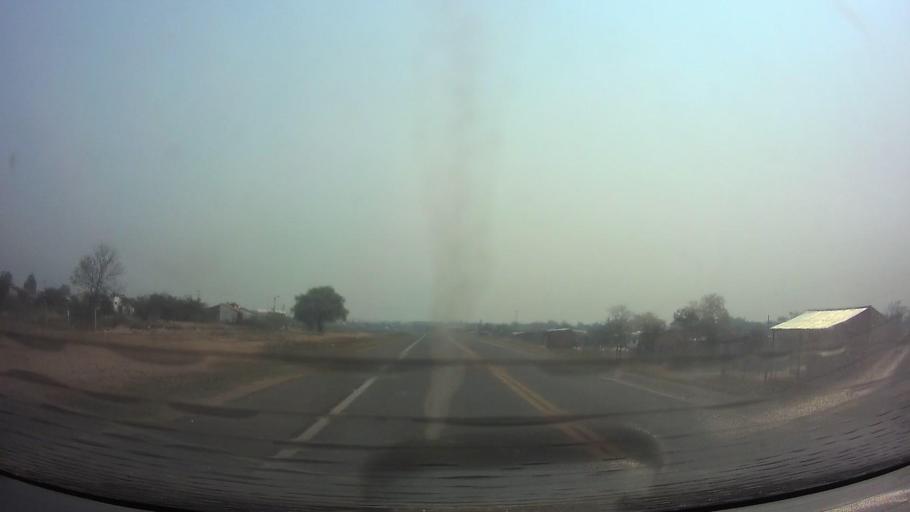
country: PY
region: Central
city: Limpio
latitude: -25.1528
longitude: -57.4820
